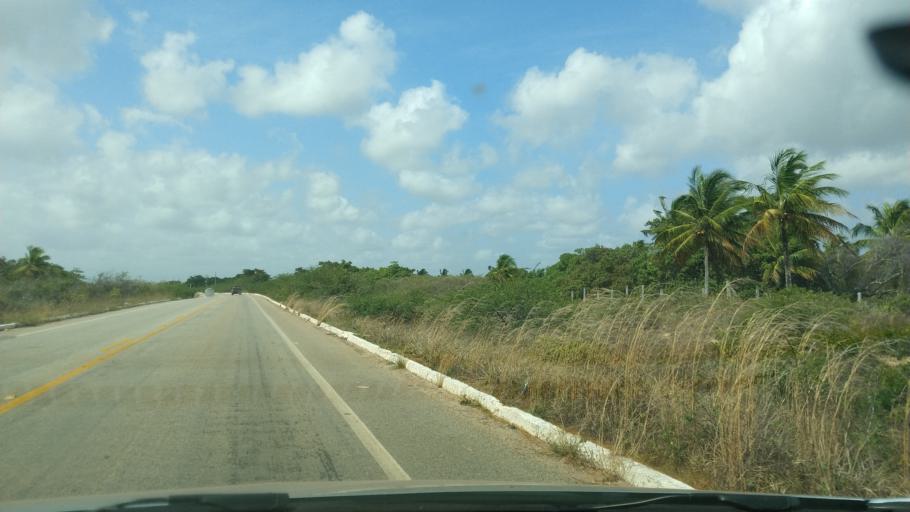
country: BR
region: Rio Grande do Norte
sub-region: Touros
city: Touros
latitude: -5.1802
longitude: -35.5108
